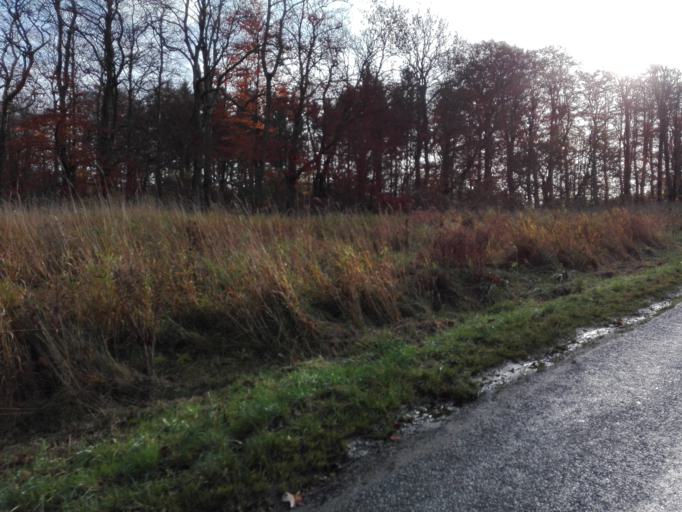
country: DK
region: Central Jutland
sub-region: Arhus Kommune
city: Beder
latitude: 56.0822
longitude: 10.2349
